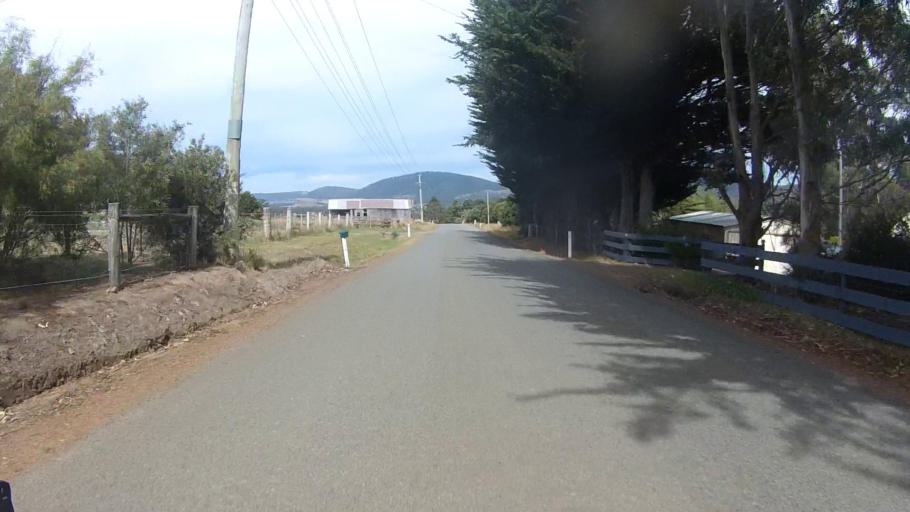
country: AU
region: Tasmania
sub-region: Sorell
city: Sorell
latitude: -42.7791
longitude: 147.8144
